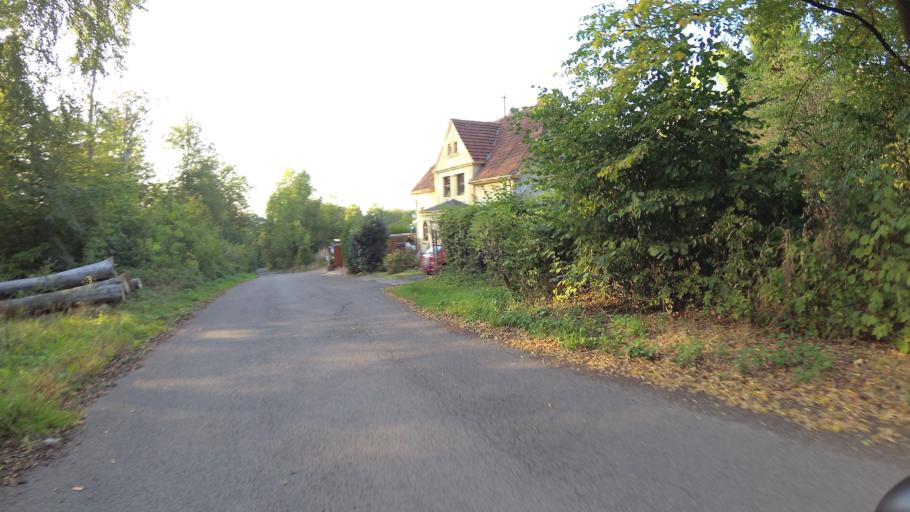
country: DE
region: Saarland
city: Sulzbach
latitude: 49.2971
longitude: 7.0849
